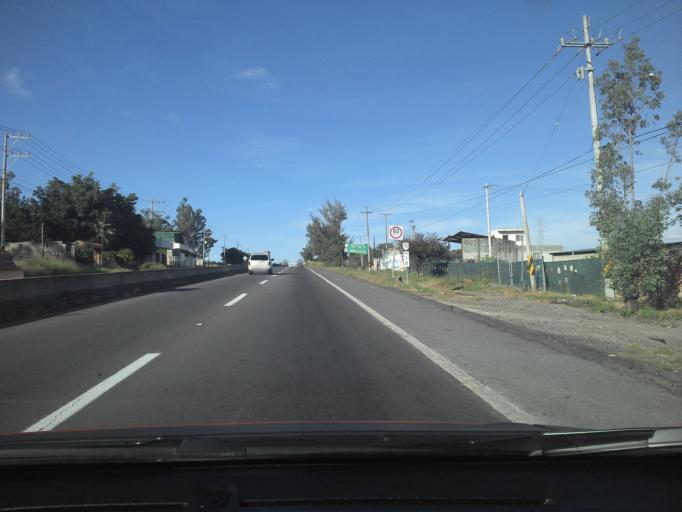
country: MX
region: Jalisco
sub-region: Tala
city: Los Ruisenores
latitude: 20.6973
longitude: -103.6898
